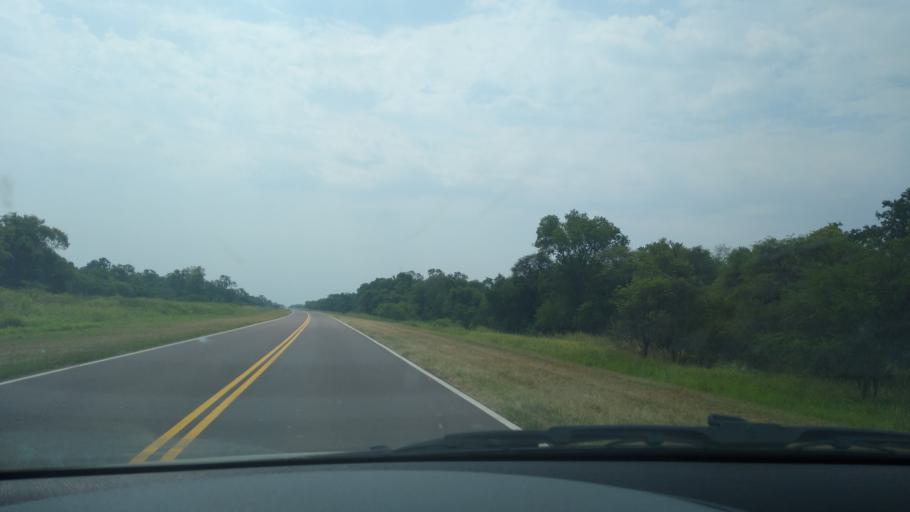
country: AR
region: Chaco
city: Margarita Belen
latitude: -27.0470
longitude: -58.9625
